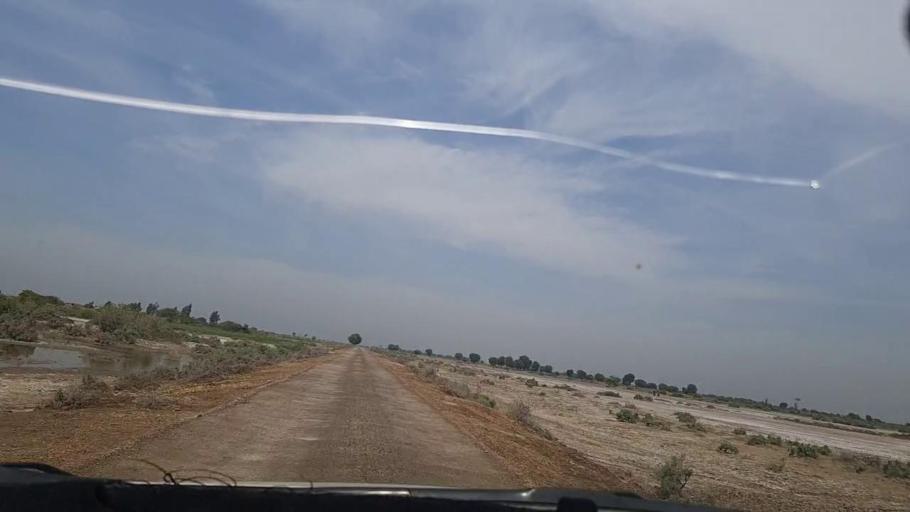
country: PK
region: Sindh
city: Pithoro
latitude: 25.4515
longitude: 69.4643
